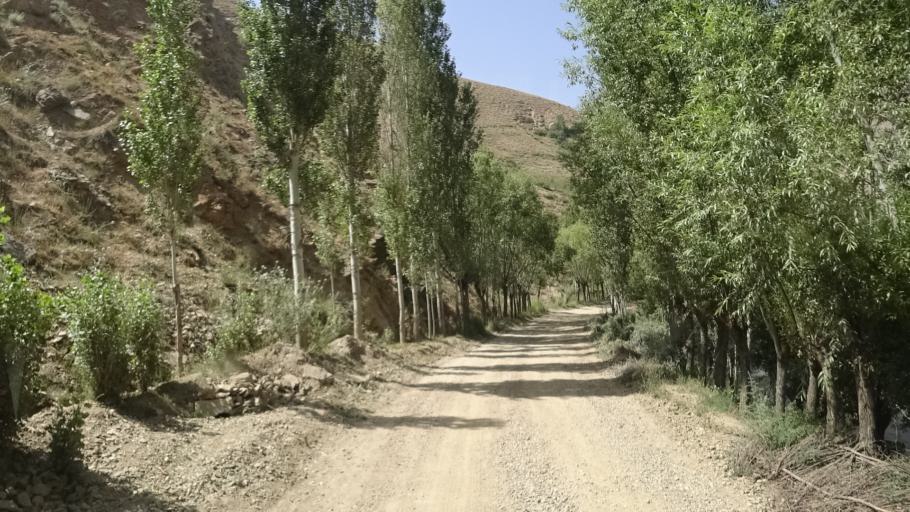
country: TJ
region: Gorno-Badakhshan
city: Khorugh
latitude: 37.1822
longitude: 71.4583
